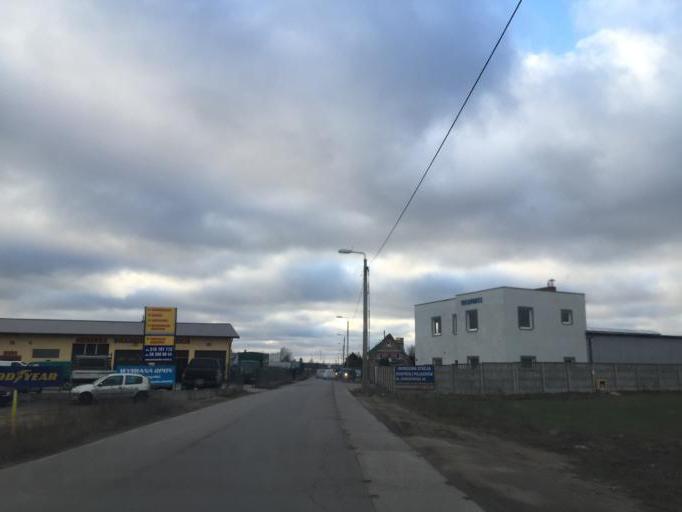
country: PL
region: Pomeranian Voivodeship
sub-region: Powiat kartuski
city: Chwaszczyno
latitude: 54.4159
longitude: 18.4636
